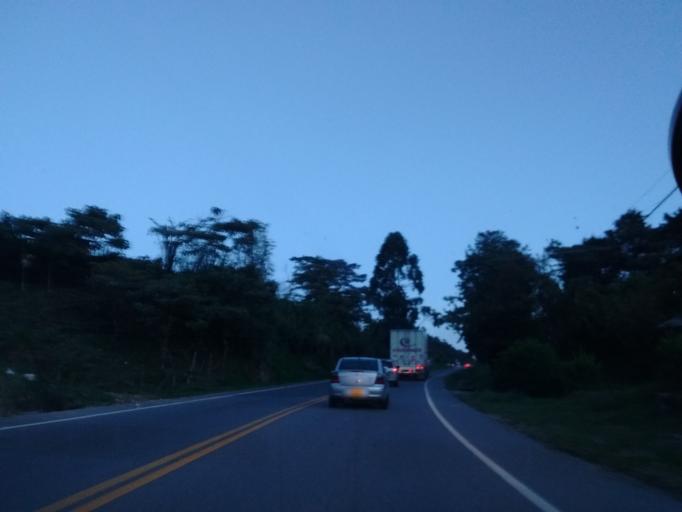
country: CO
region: Antioquia
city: Santuario
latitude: 6.1175
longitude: -75.2328
